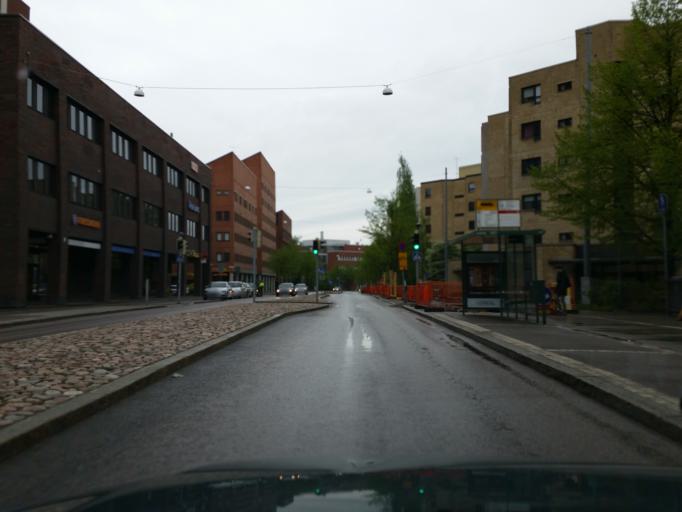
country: FI
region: Uusimaa
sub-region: Helsinki
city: Teekkarikylae
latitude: 60.2308
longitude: 24.8819
